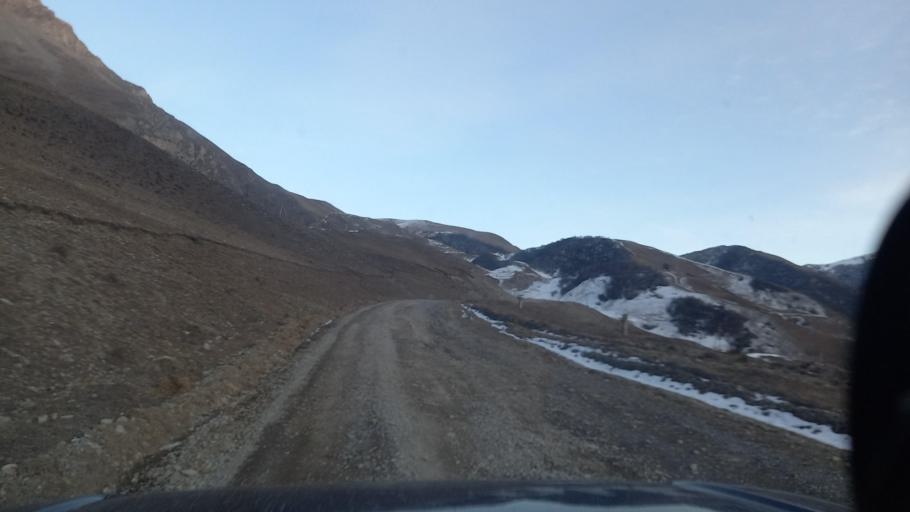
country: RU
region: Ingushetiya
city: Dzhayrakh
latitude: 42.8399
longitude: 44.5413
